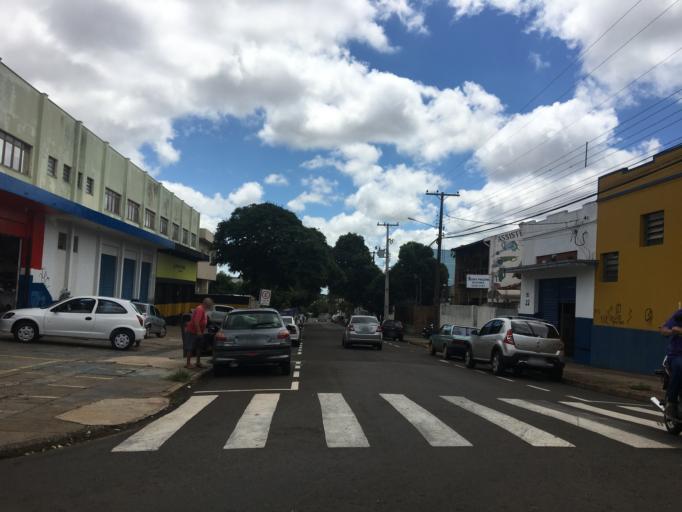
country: BR
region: Parana
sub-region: Londrina
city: Londrina
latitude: -23.3001
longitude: -51.1628
